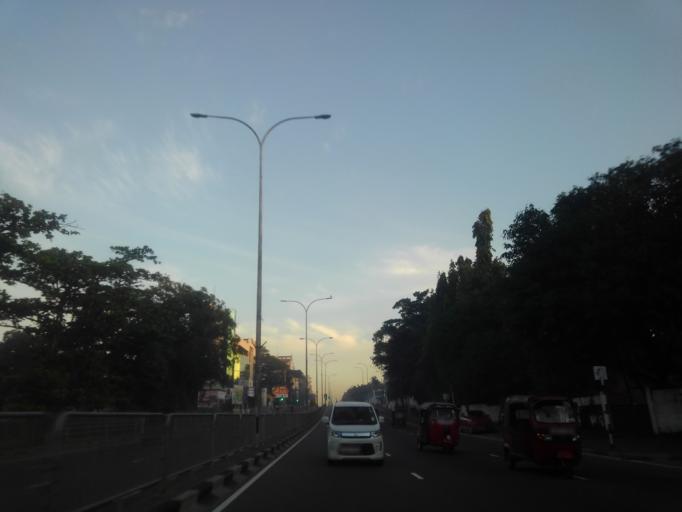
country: LK
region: Western
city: Kolonnawa
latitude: 6.9196
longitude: 79.8778
